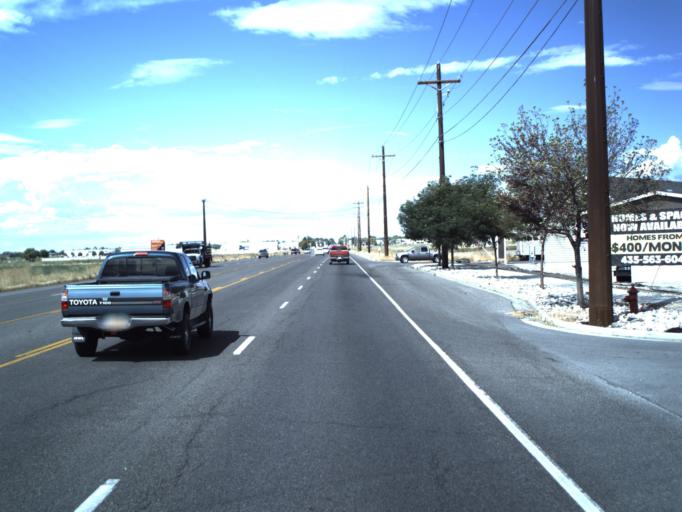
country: US
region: Utah
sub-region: Cache County
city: Hyde Park
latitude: 41.8067
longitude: -111.8333
